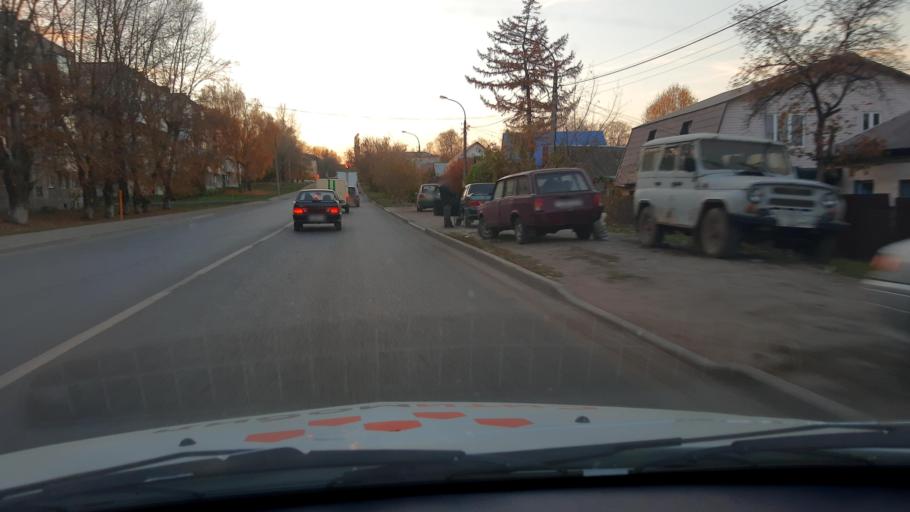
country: RU
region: Bashkortostan
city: Ufa
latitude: 54.8217
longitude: 56.1158
